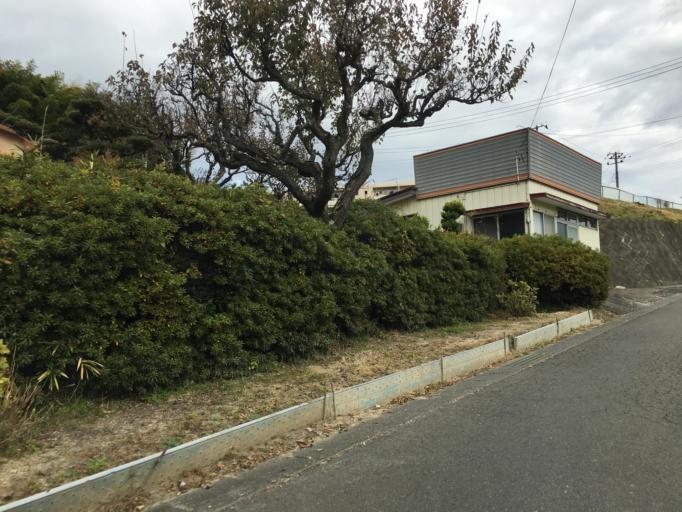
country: JP
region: Fukushima
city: Nihommatsu
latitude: 37.6019
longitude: 140.4350
